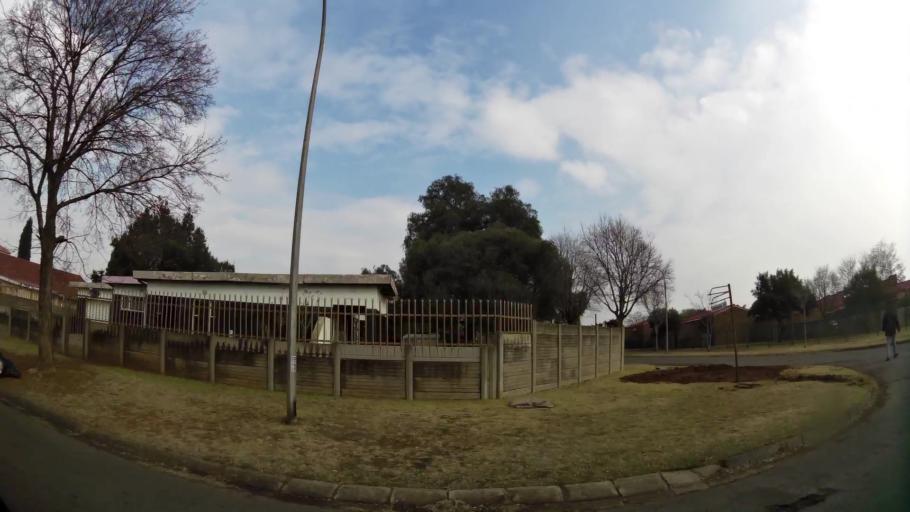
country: ZA
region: Gauteng
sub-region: Sedibeng District Municipality
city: Vanderbijlpark
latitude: -26.6944
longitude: 27.8510
